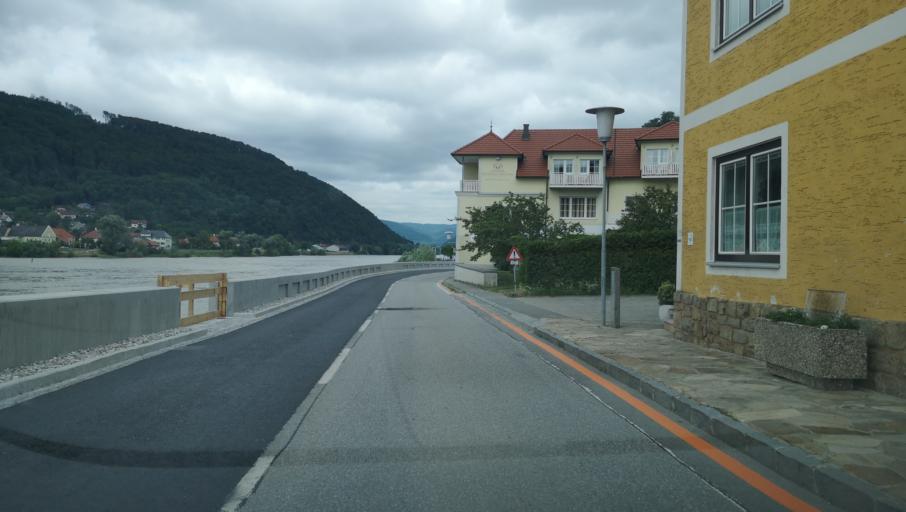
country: AT
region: Lower Austria
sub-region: Politischer Bezirk Krems
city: Aggsbach
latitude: 48.2902
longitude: 15.4067
